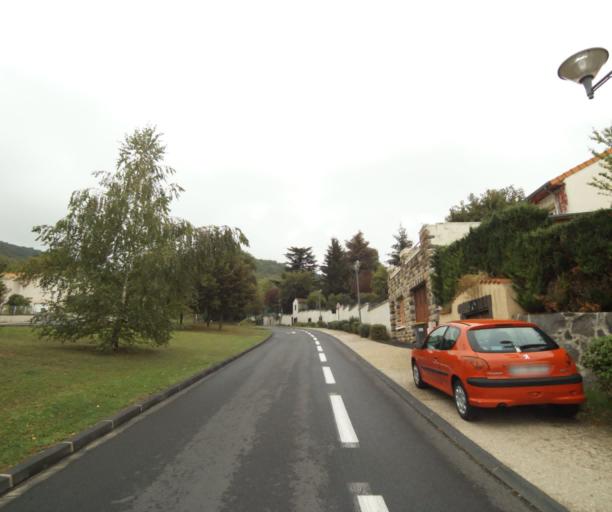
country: FR
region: Auvergne
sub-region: Departement du Puy-de-Dome
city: Romagnat
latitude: 45.7263
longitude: 3.1011
